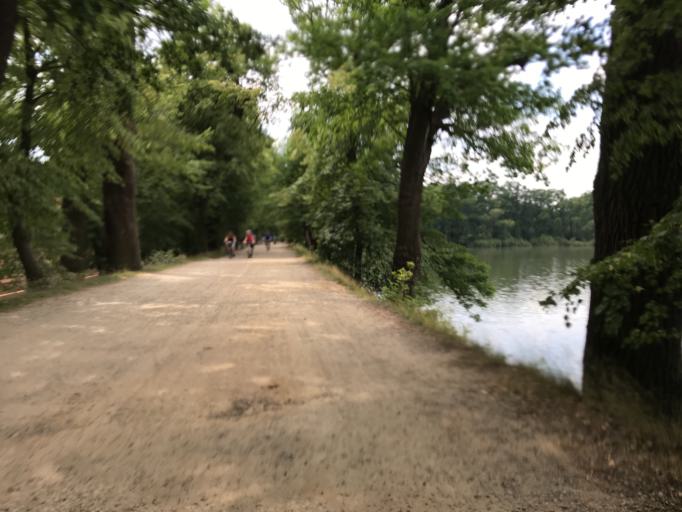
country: CZ
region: Jihocesky
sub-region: Okres Jindrichuv Hradec
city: Trebon
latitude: 48.9973
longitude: 14.7720
